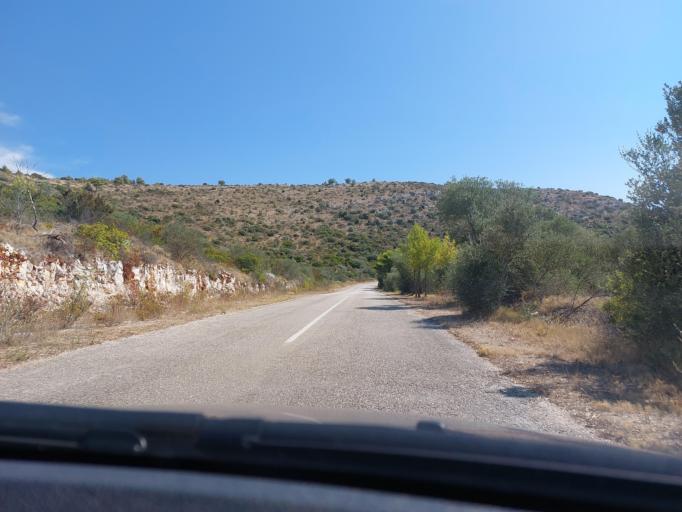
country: HR
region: Dubrovacko-Neretvanska
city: Smokvica
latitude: 42.7504
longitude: 16.8784
